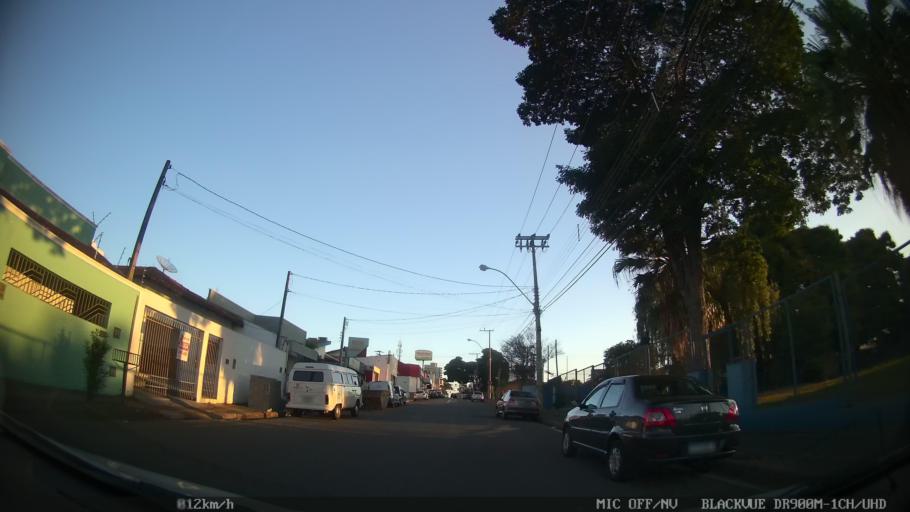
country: BR
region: Sao Paulo
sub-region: Santa Barbara D'Oeste
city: Santa Barbara d'Oeste
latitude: -22.7508
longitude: -47.4131
